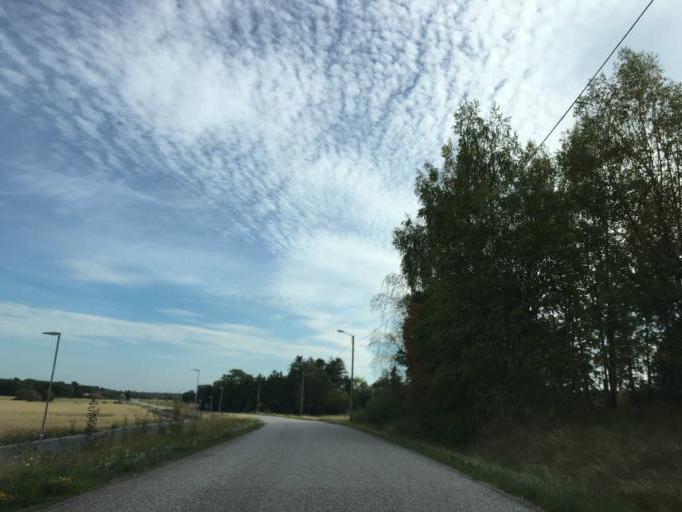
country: SE
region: Soedermanland
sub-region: Eskilstuna Kommun
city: Torshalla
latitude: 59.4463
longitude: 16.4688
